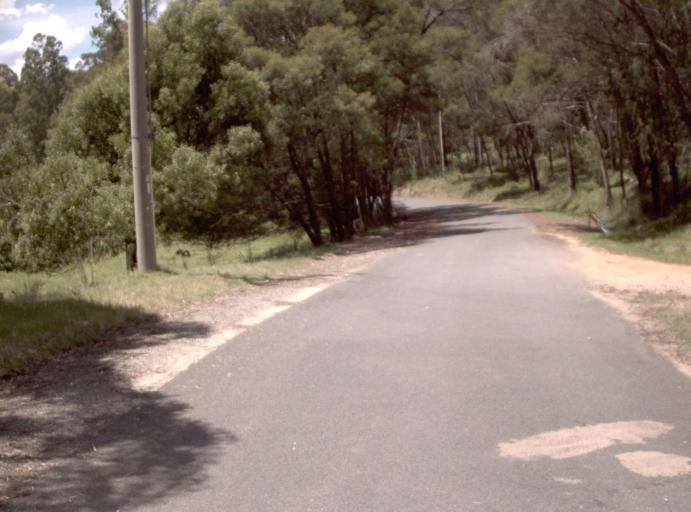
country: AU
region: New South Wales
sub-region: Bombala
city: Bombala
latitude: -37.4333
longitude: 148.9992
